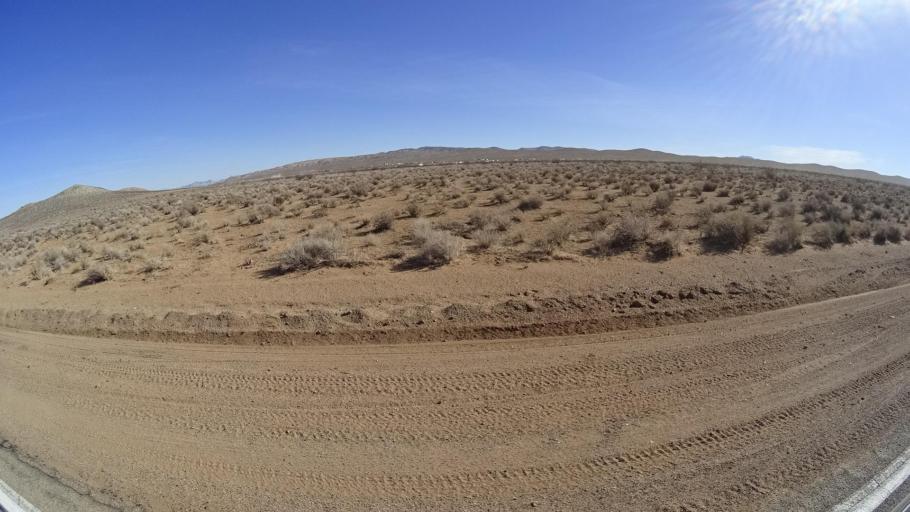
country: US
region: California
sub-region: Kern County
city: Ridgecrest
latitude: 35.4915
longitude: -117.6305
